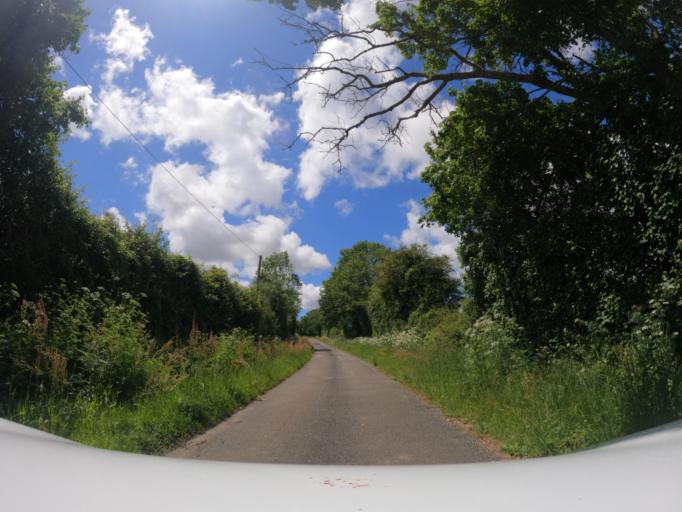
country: FR
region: Pays de la Loire
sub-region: Departement de la Vendee
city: Le Champ-Saint-Pere
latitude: 46.4951
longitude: -1.3578
